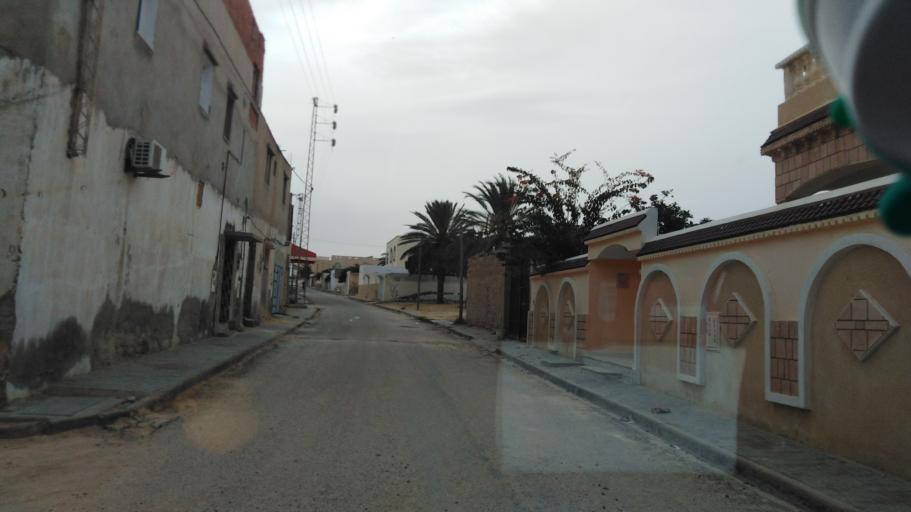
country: TN
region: Qabis
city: Gabes
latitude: 33.9563
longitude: 10.0044
